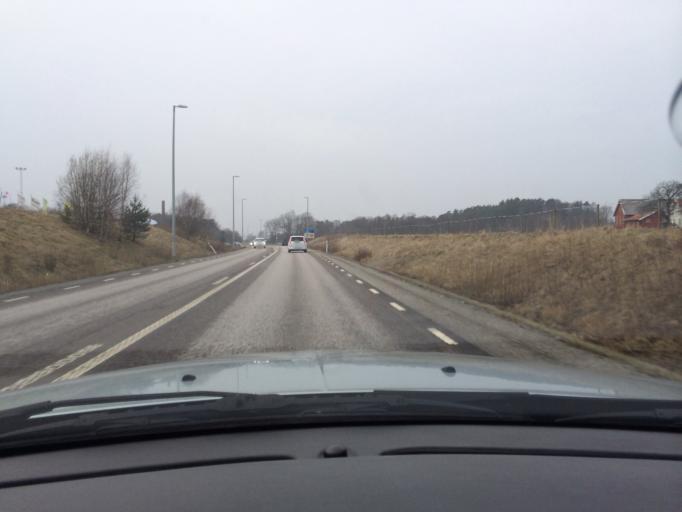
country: SE
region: Vaestra Goetaland
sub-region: Stenungsunds Kommun
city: Stenungsund
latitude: 58.0683
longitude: 11.8598
